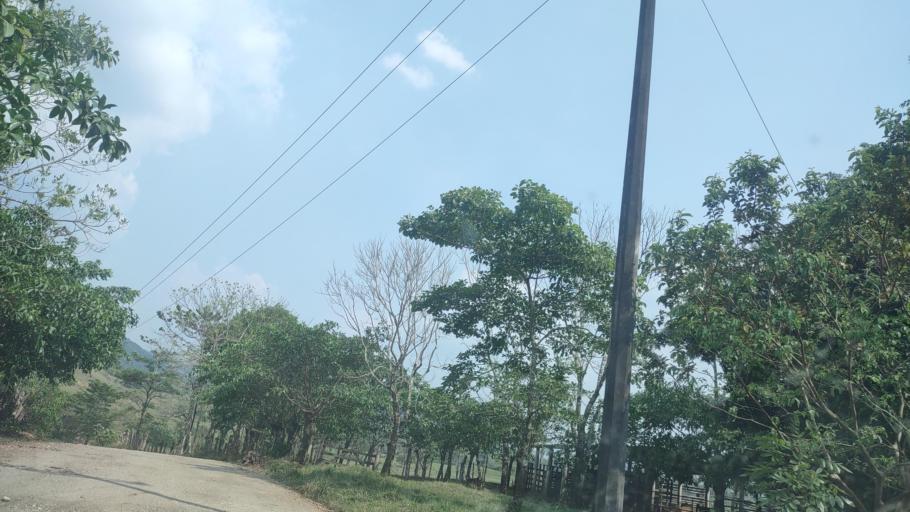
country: MX
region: Chiapas
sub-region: Tecpatan
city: Raudales Malpaso
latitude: 17.4240
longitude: -93.7939
